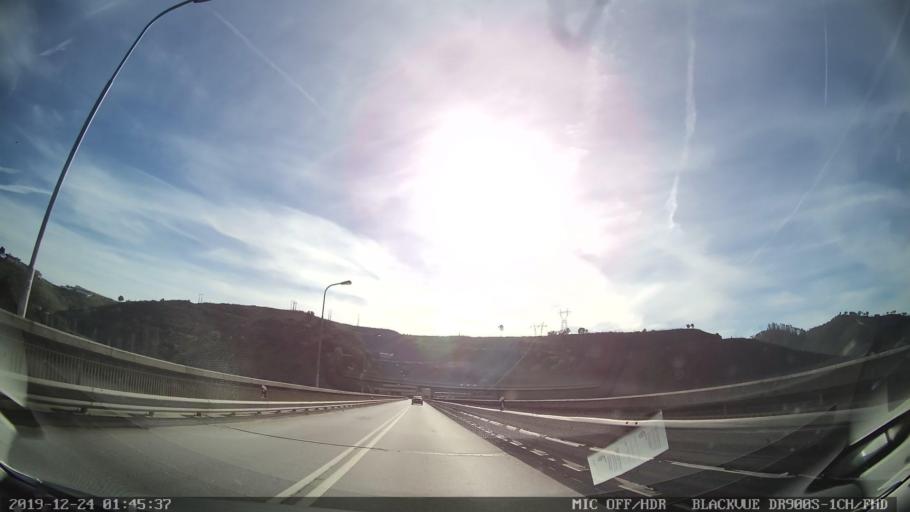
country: PT
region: Portalegre
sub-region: Gaviao
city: Gaviao
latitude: 39.5442
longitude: -7.8029
